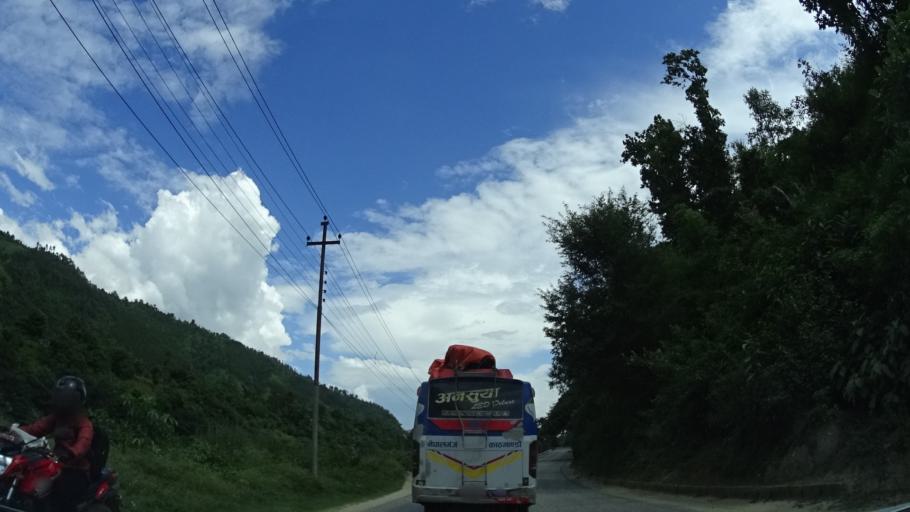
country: NP
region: Central Region
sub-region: Narayani Zone
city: Hitura
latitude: 27.8079
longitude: 84.8517
